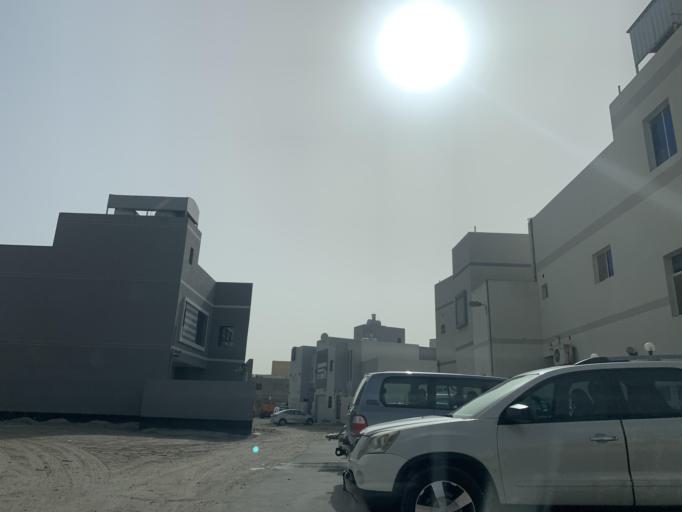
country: BH
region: Northern
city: Sitrah
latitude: 26.1361
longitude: 50.5963
